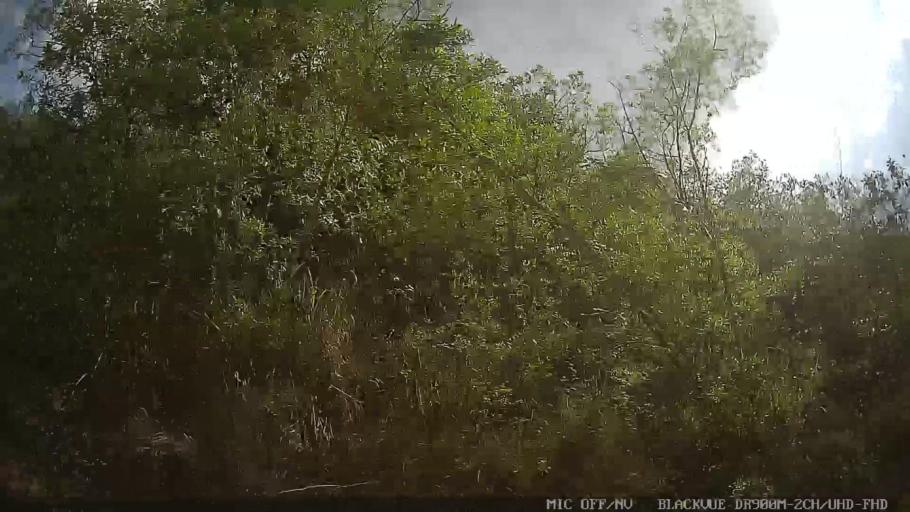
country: BR
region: Sao Paulo
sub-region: Louveira
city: Louveira
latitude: -23.0879
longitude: -46.9396
